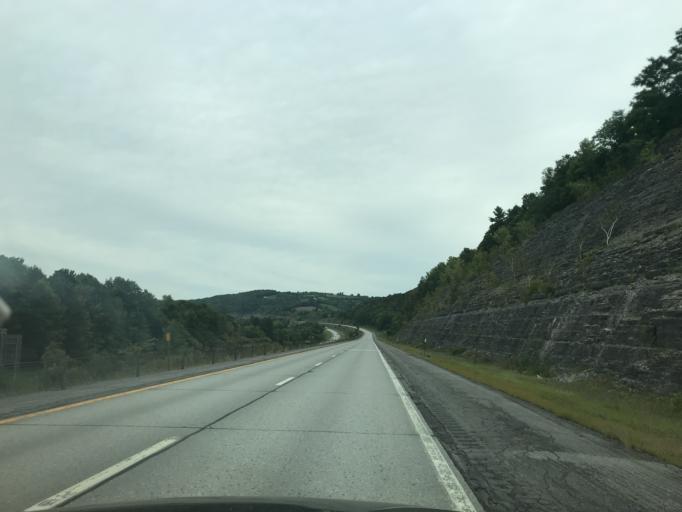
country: US
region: New York
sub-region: Schoharie County
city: Schoharie
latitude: 42.6798
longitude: -74.3926
